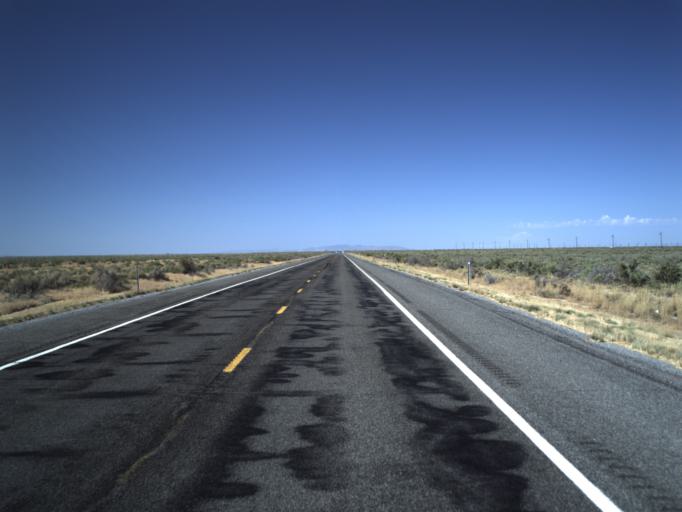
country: US
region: Utah
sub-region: Millard County
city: Delta
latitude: 39.4385
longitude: -112.4580
